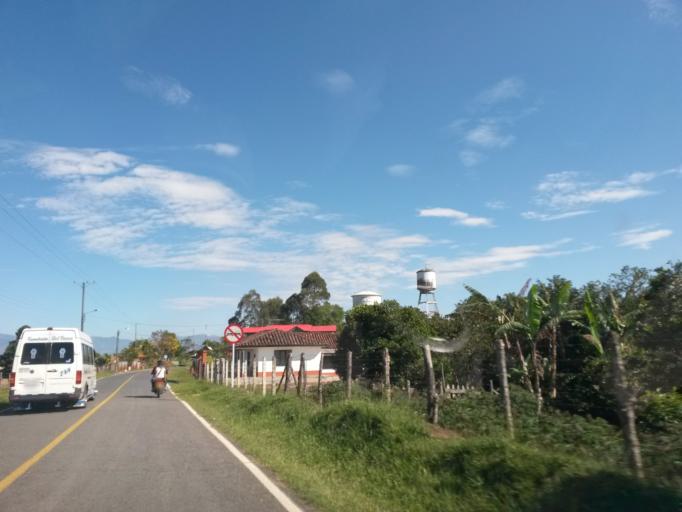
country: CO
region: Cauca
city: Morales
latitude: 2.7446
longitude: -76.6204
